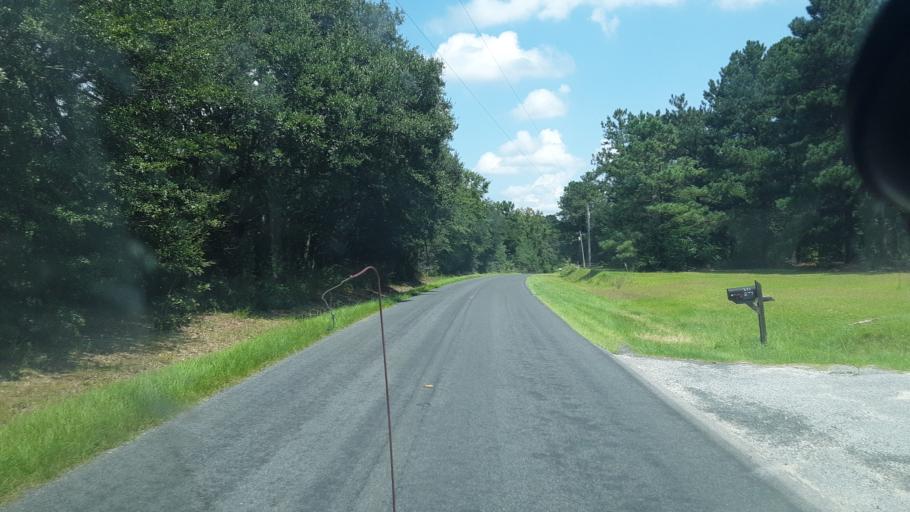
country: US
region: South Carolina
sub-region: Calhoun County
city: Oak Grove
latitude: 33.6894
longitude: -80.9675
